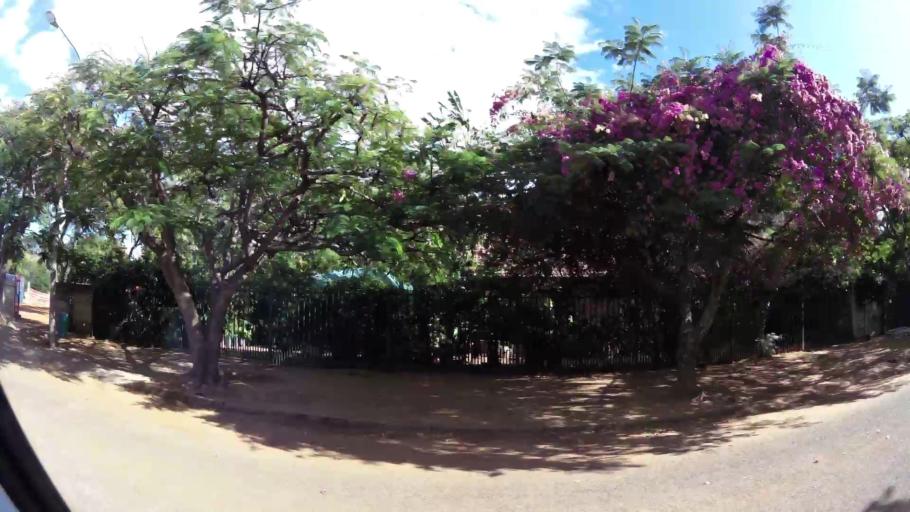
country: ZA
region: Limpopo
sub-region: Waterberg District Municipality
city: Warmbaths
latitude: -24.8751
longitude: 28.2894
